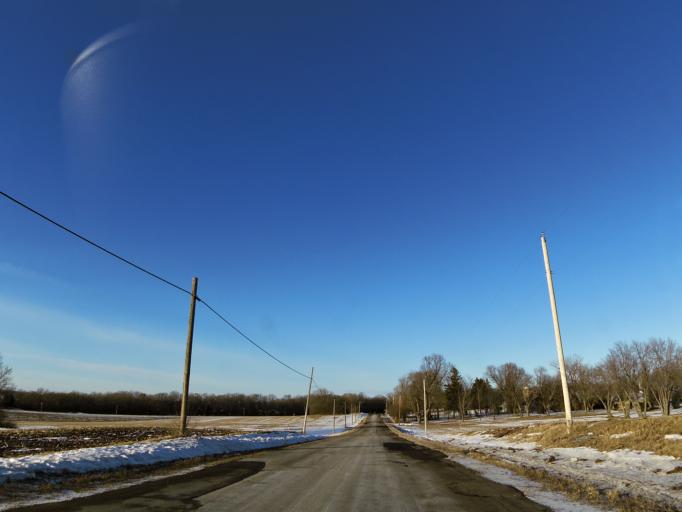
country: US
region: Minnesota
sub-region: Washington County
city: Cottage Grove
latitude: 44.8277
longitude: -92.8831
